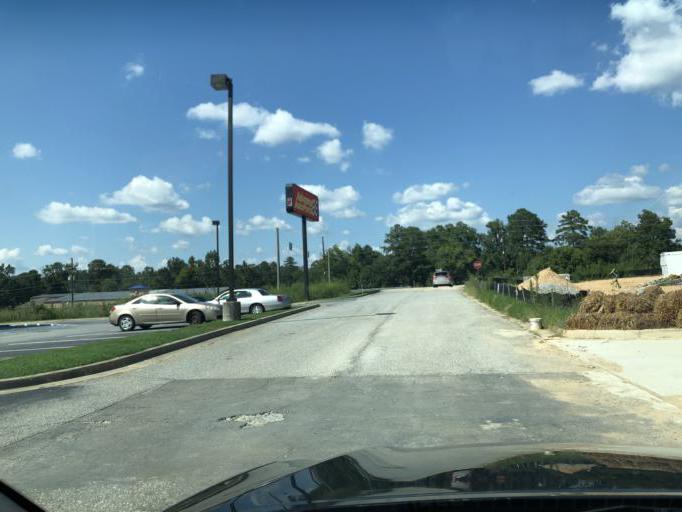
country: US
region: Georgia
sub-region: Muscogee County
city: Columbus
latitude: 32.5225
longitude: -84.9168
